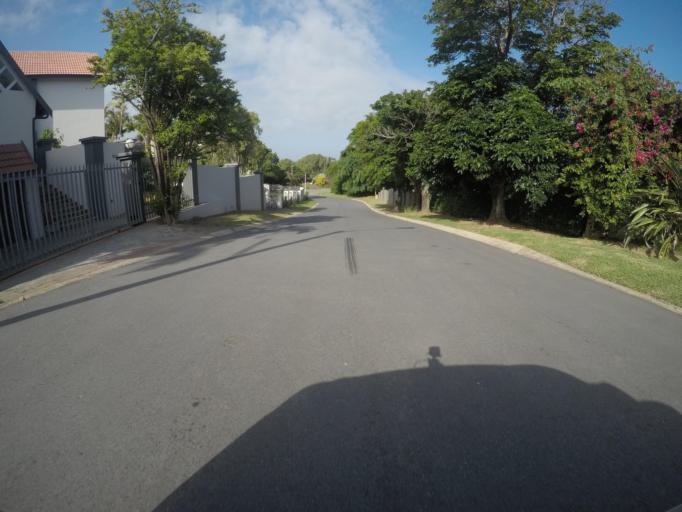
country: ZA
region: Eastern Cape
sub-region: Buffalo City Metropolitan Municipality
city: East London
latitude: -32.9728
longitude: 27.9546
